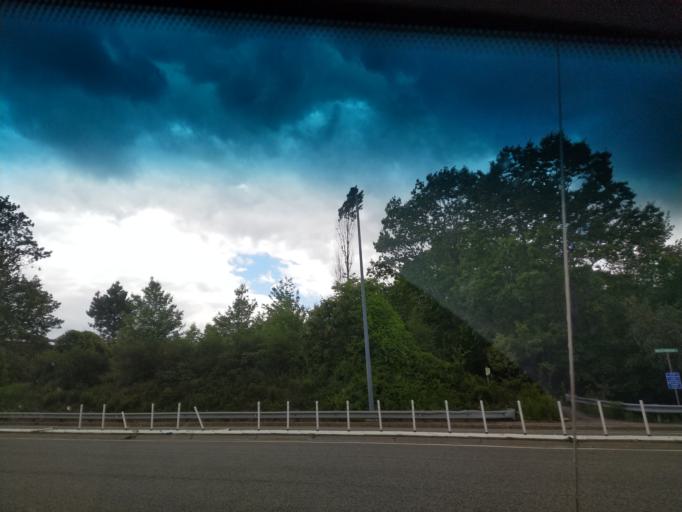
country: US
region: Maine
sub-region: Cumberland County
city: South Portland Gardens
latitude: 43.6318
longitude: -70.3122
